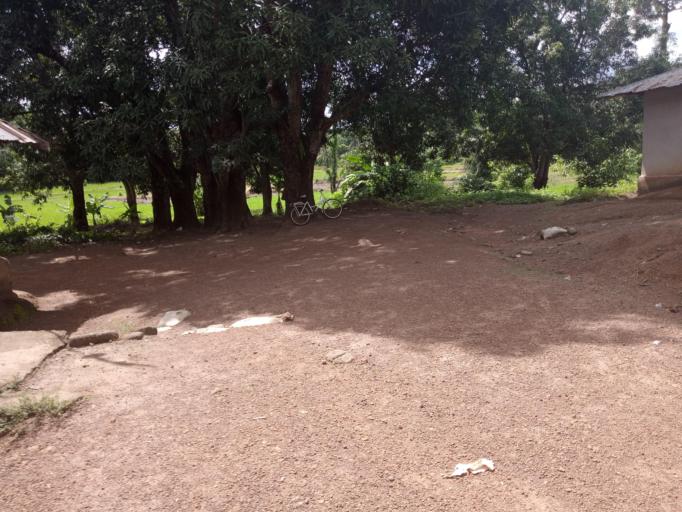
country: SL
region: Northern Province
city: Kamakwie
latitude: 9.4948
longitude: -12.2469
